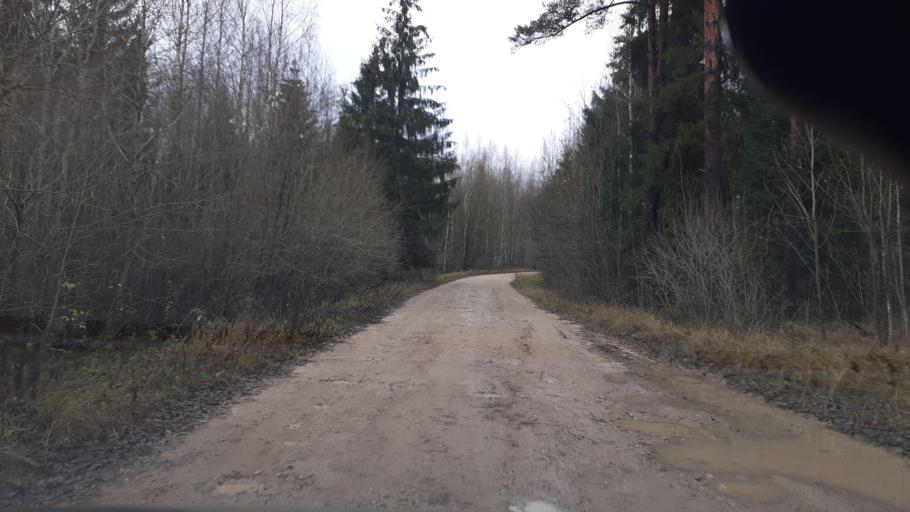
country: LV
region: Kuldigas Rajons
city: Kuldiga
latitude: 57.0284
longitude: 21.8698
